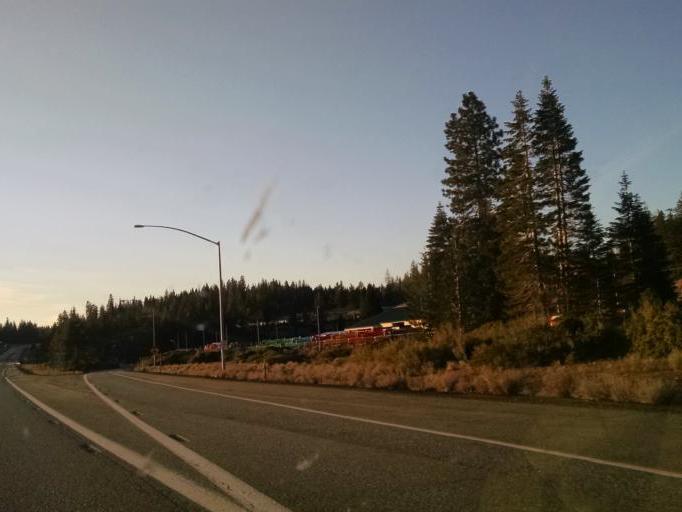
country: US
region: California
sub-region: Siskiyou County
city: Weed
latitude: 41.3659
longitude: -122.3677
